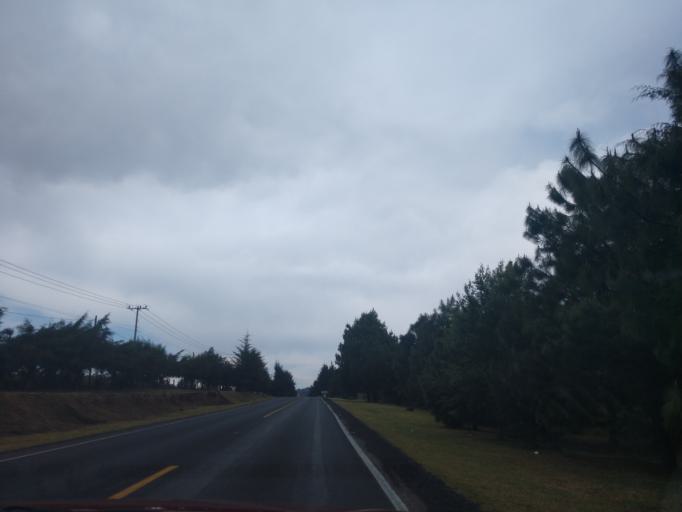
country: MX
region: Jalisco
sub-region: Mazamitla
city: Mazamitla
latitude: 19.9284
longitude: -103.0419
